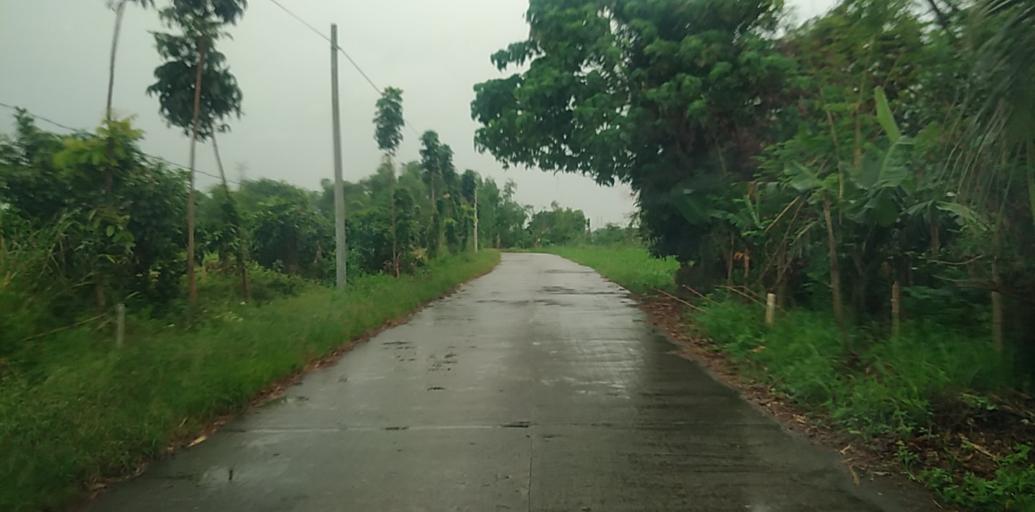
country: PH
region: Central Luzon
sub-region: Province of Pampanga
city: San Antonio
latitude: 15.1532
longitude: 120.6825
